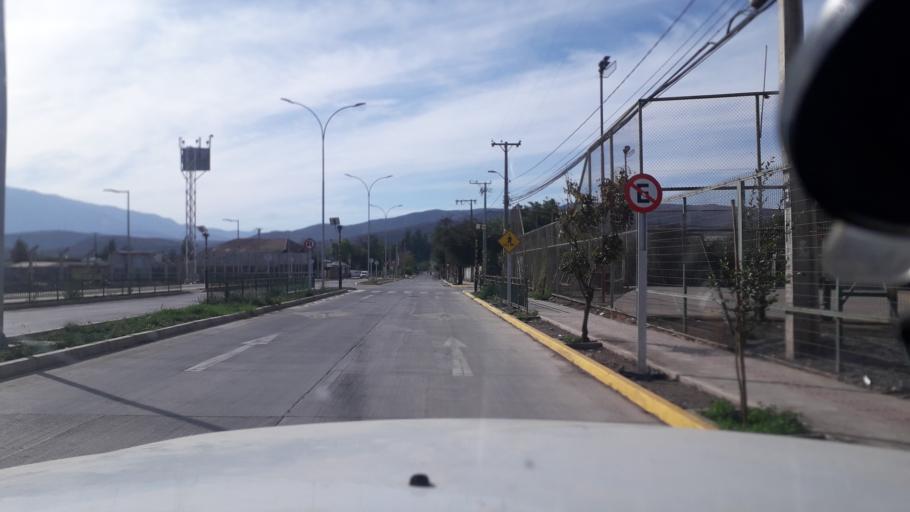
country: CL
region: Valparaiso
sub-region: Provincia de San Felipe
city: San Felipe
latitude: -32.7440
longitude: -70.7107
